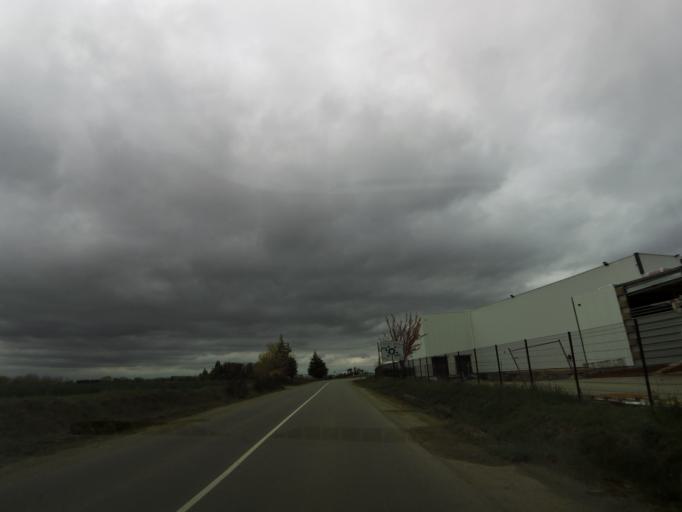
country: FR
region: Brittany
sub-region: Departement d'Ille-et-Vilaine
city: Janze
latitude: 47.9686
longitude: -1.5357
